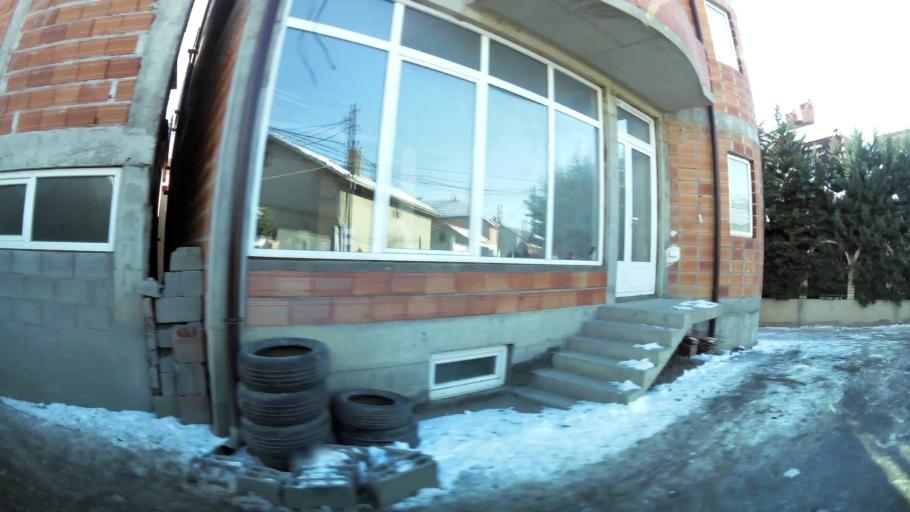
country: MK
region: Saraj
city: Saraj
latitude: 42.0004
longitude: 21.3211
